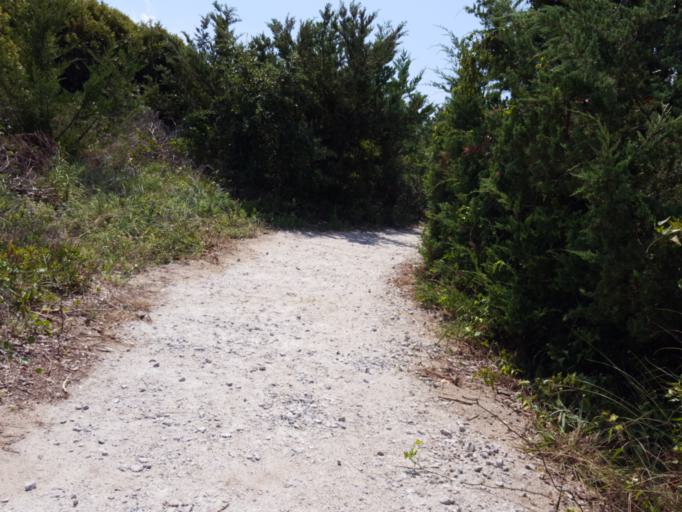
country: US
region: North Carolina
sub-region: Carteret County
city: Beaufort
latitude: 34.6961
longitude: -76.6774
